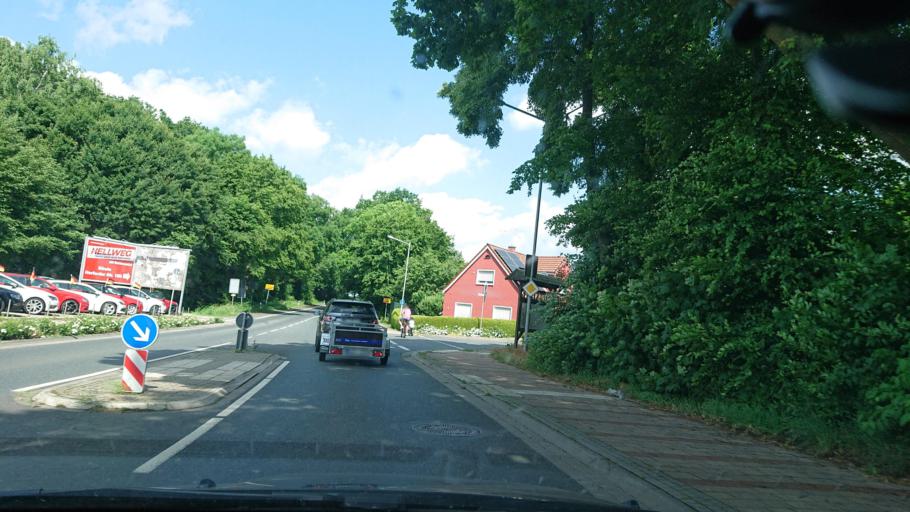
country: DE
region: North Rhine-Westphalia
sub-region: Regierungsbezirk Detmold
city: Hiddenhausen
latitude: 52.1693
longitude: 8.6262
